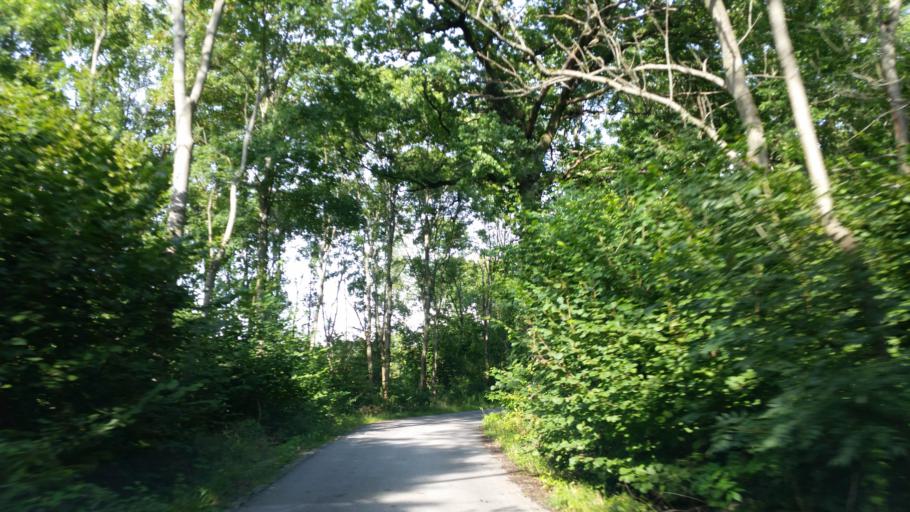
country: DE
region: Saxony
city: Sohland am Rotstein
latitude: 51.1118
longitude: 14.7533
